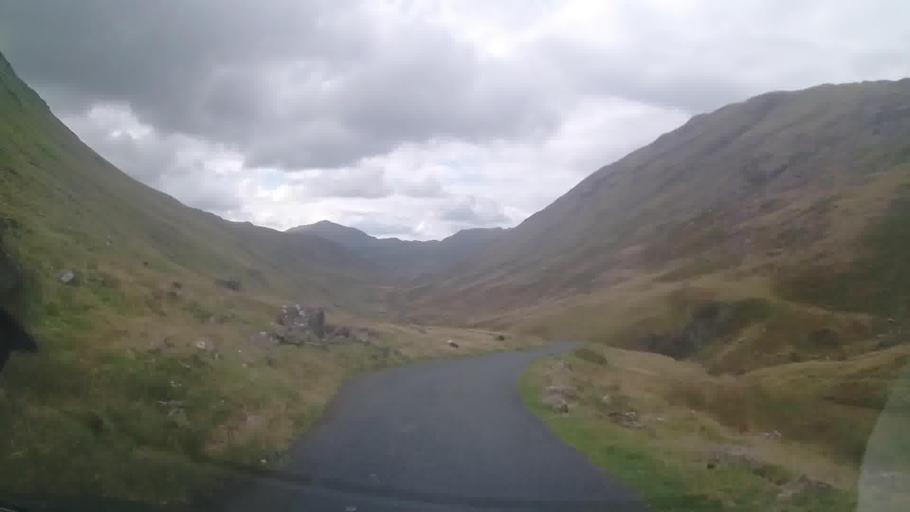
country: GB
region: England
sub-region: Cumbria
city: Ambleside
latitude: 54.4139
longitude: -3.1209
